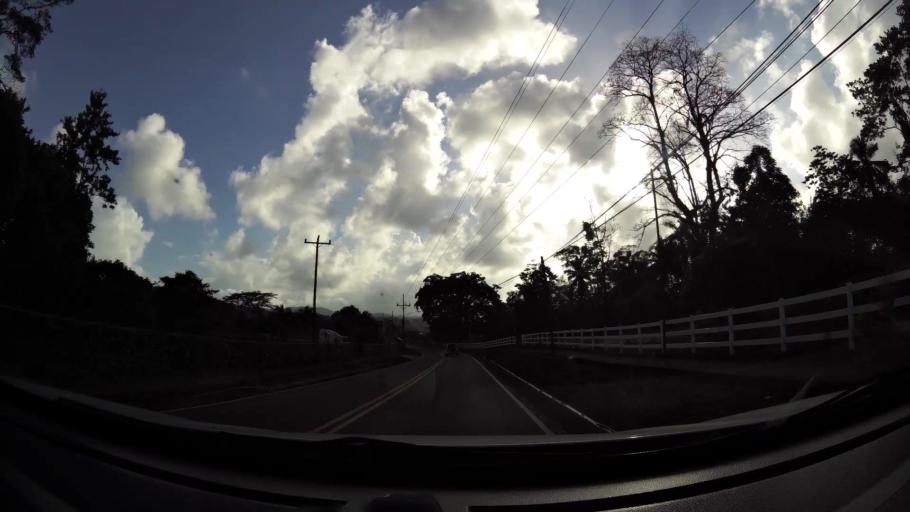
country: CR
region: Limon
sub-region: Canton de Siquirres
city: Siquirres
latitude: 10.0919
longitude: -83.5402
